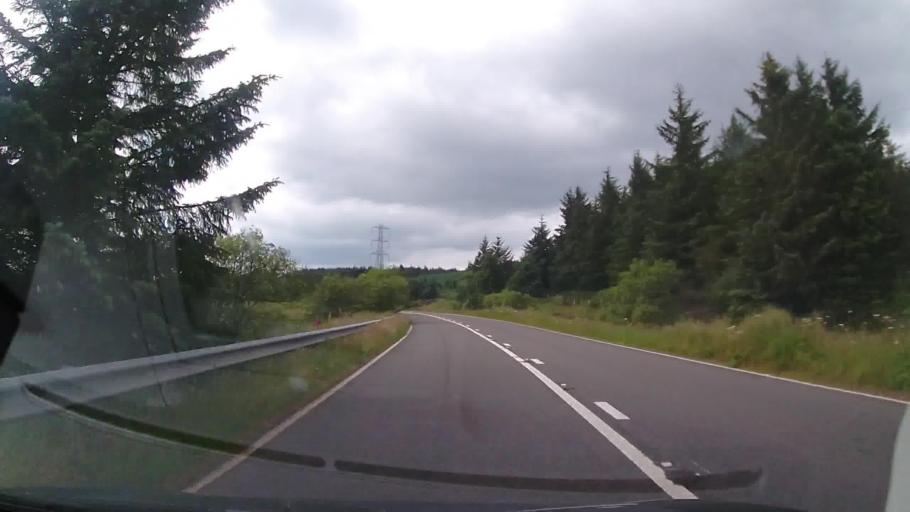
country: GB
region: Wales
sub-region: Gwynedd
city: Trawsfynydd
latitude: 52.9312
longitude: -3.8027
